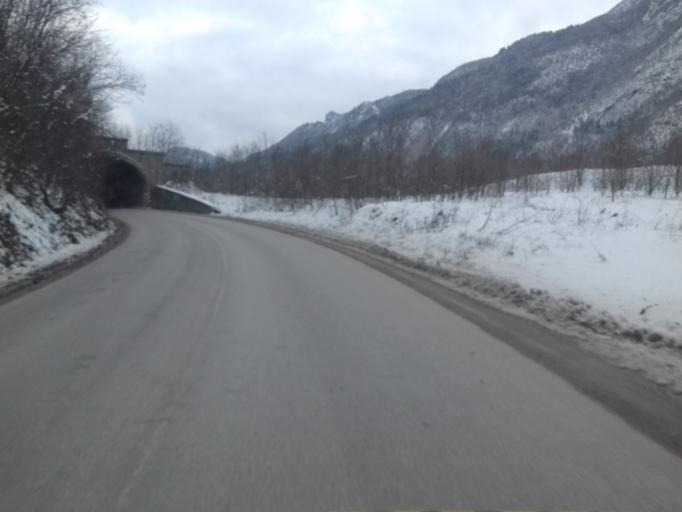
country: BA
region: Federation of Bosnia and Herzegovina
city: Kobilja Glava
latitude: 43.8493
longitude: 18.4649
